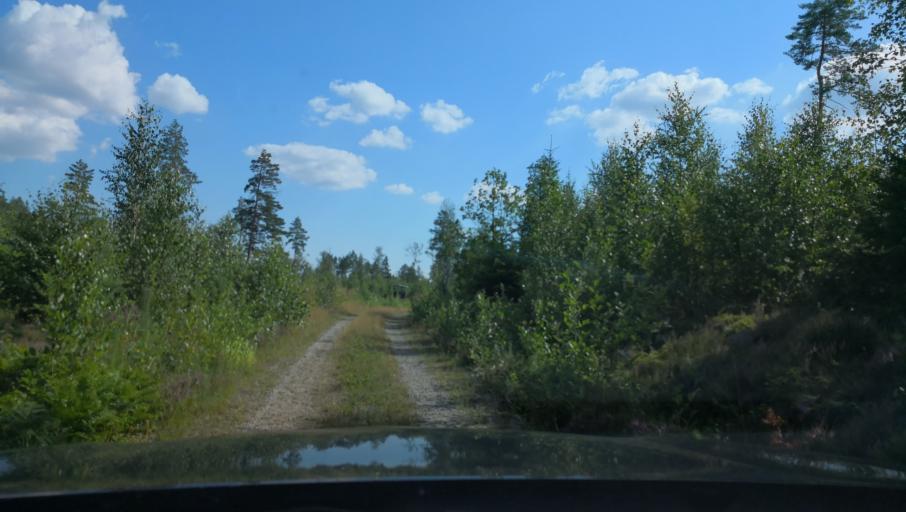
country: SE
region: Vaestmanland
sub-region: Vasteras
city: Skultuna
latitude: 59.7173
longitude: 16.3868
